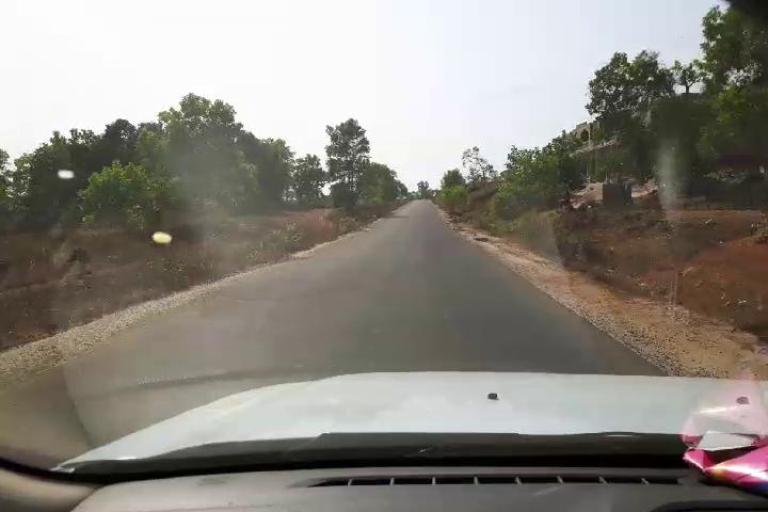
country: SL
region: Western Area
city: Hastings
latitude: 8.3136
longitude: -13.1878
